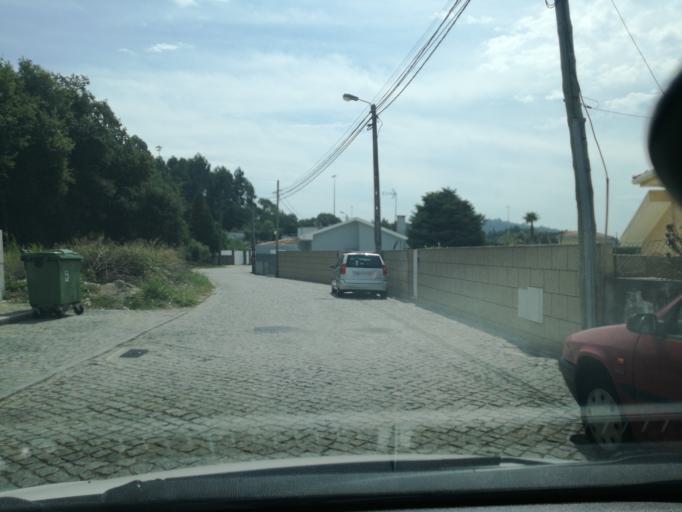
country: PT
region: Porto
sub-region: Vila Nova de Gaia
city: Grijo
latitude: 41.0178
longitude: -8.5850
